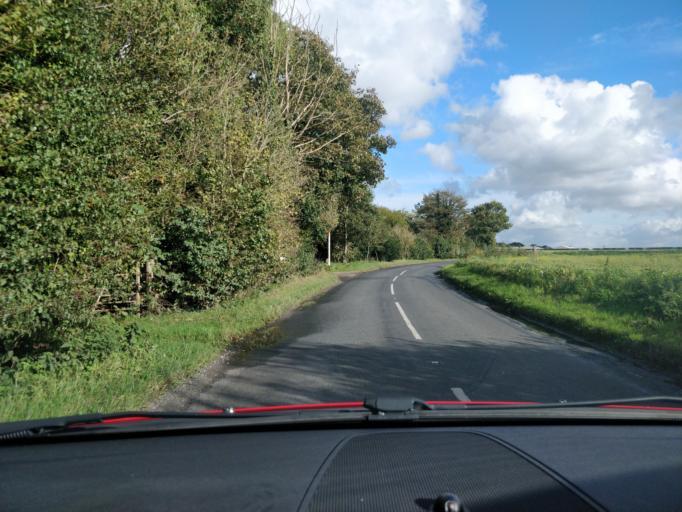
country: GB
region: England
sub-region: Lancashire
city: Parbold
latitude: 53.5884
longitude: -2.8263
